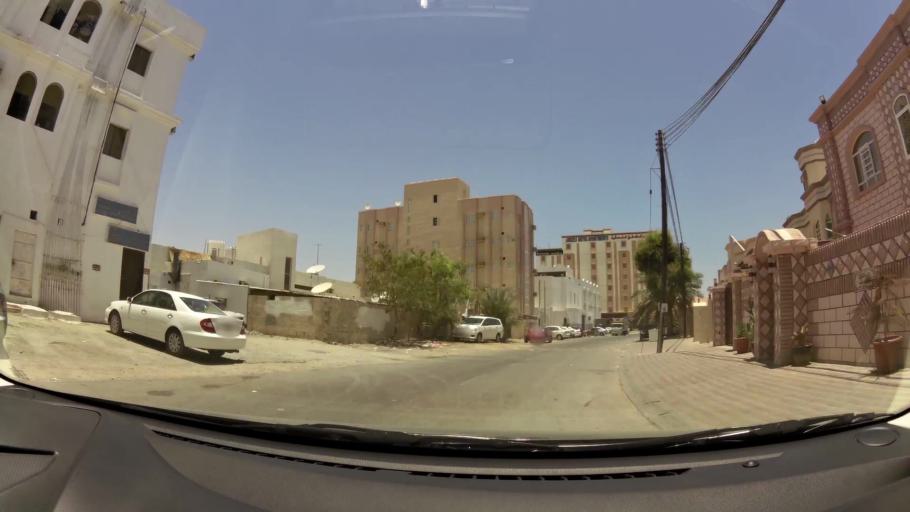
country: OM
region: Muhafazat Masqat
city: As Sib al Jadidah
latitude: 23.6295
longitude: 58.2351
